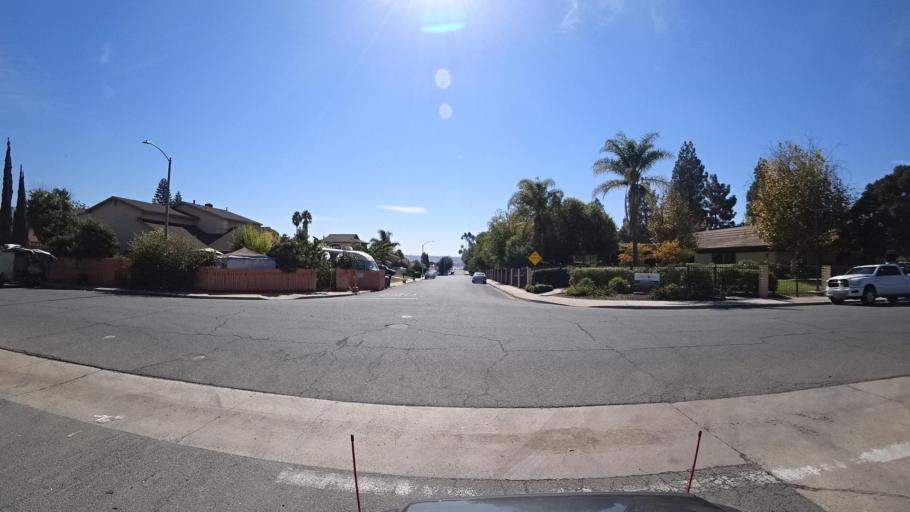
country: US
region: California
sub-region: San Diego County
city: La Presa
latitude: 32.7043
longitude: -116.9989
